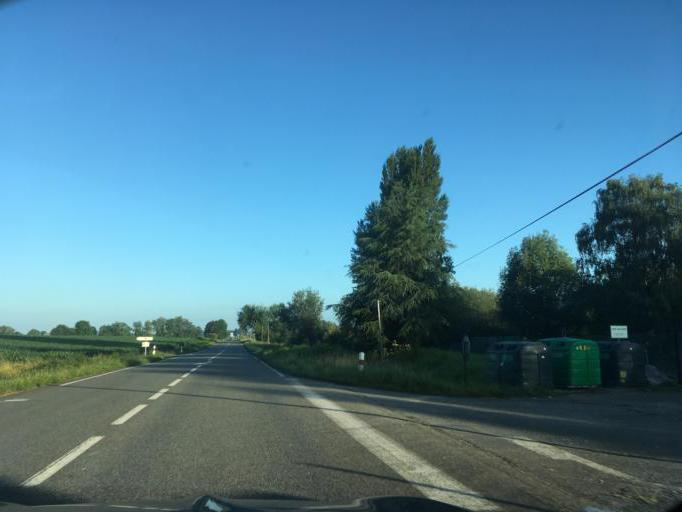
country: FR
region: Aquitaine
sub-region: Departement des Pyrenees-Atlantiques
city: Soumoulou
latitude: 43.2557
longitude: -0.1416
